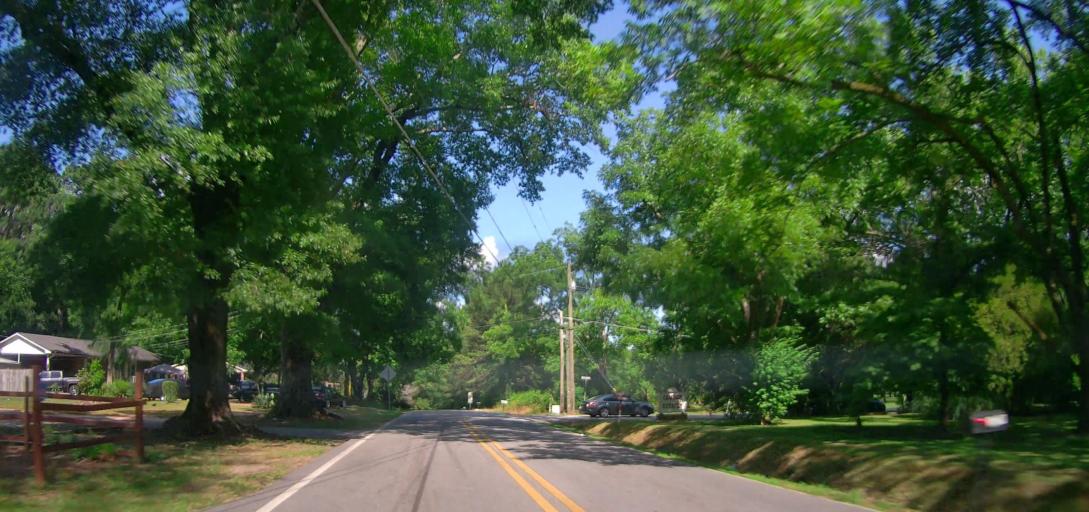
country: US
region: Georgia
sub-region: Spalding County
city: East Griffin
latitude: 33.2830
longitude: -84.2257
